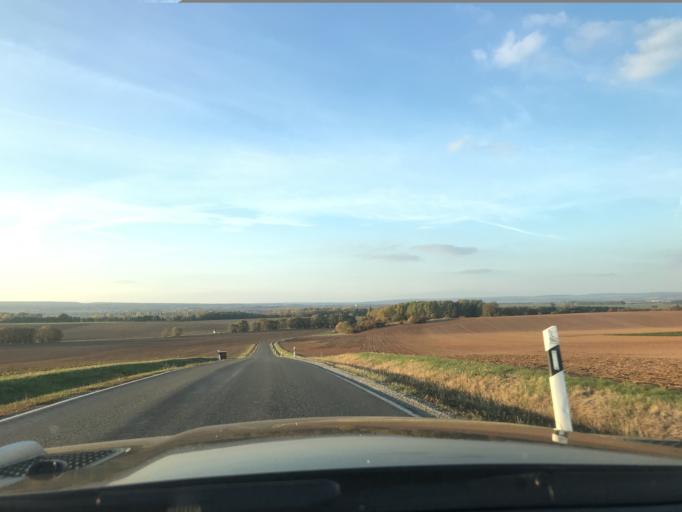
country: DE
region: Thuringia
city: Flarchheim
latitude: 51.1327
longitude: 10.4720
